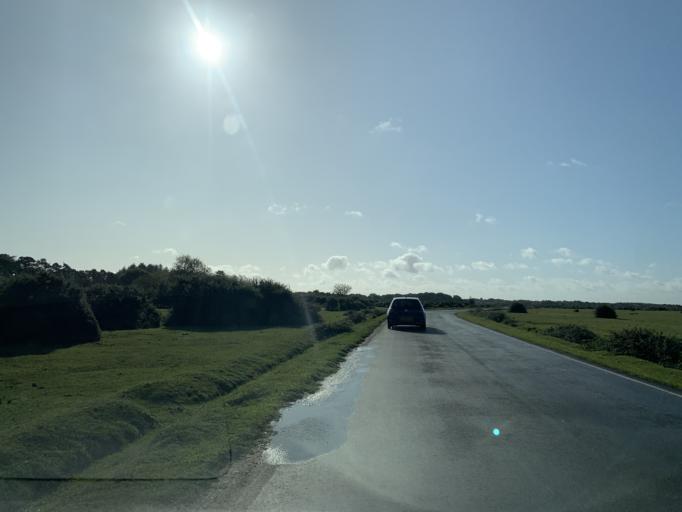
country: GB
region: England
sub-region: Hampshire
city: Cadnam
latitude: 50.9207
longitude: -1.6518
